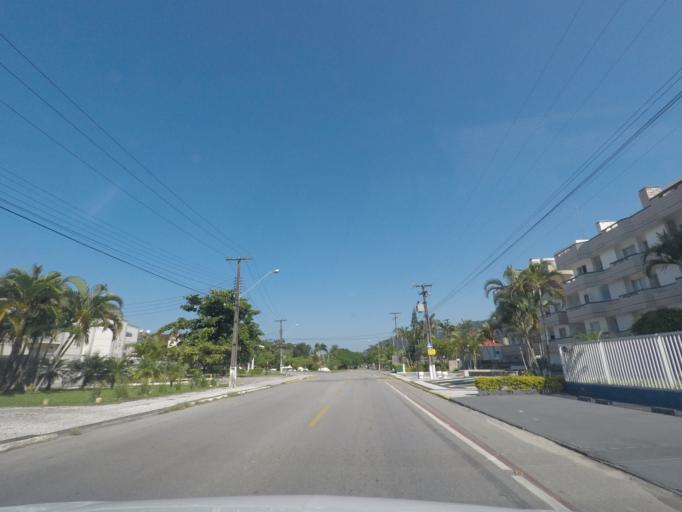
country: BR
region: Parana
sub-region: Guaratuba
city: Guaratuba
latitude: -25.8320
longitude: -48.5397
